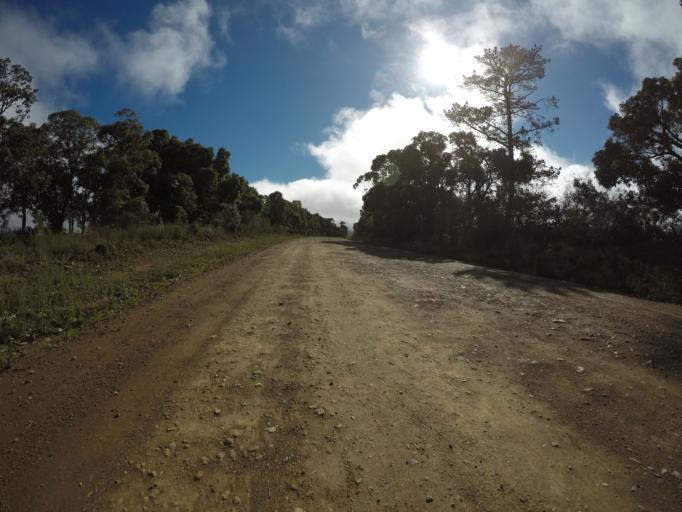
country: ZA
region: Western Cape
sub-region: Cape Winelands District Municipality
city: Ashton
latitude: -34.1171
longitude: 19.8049
